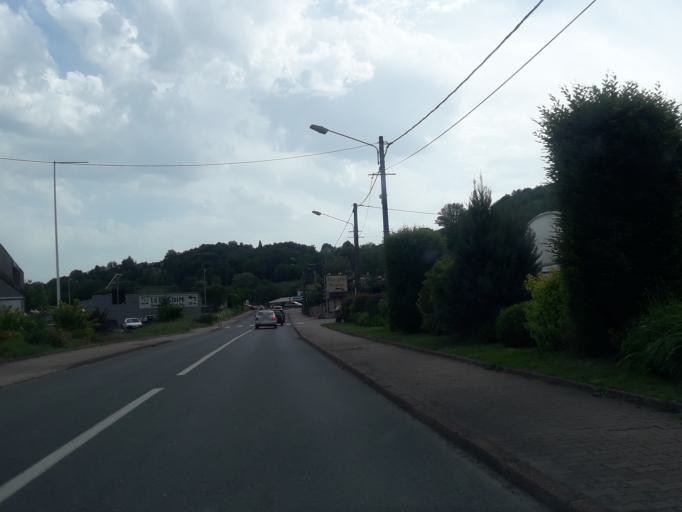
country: FR
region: Rhone-Alpes
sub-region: Departement du Rhone
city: Sain-Bel
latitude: 45.8267
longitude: 4.6077
